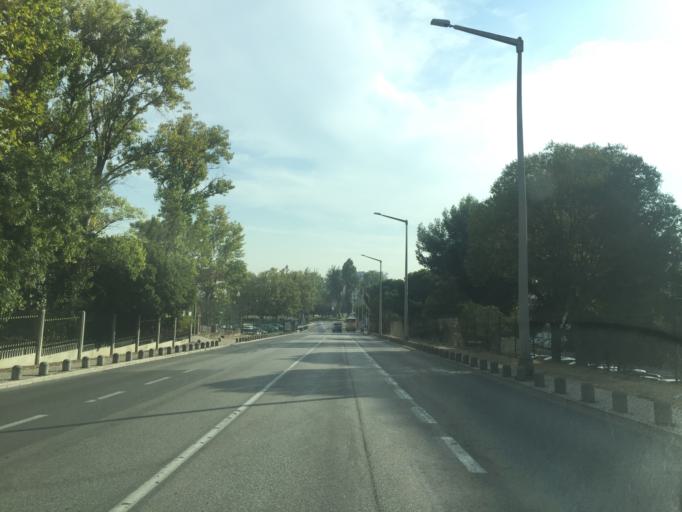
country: PT
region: Lisbon
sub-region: Loures
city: Moscavide
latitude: 38.7757
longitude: -9.1264
